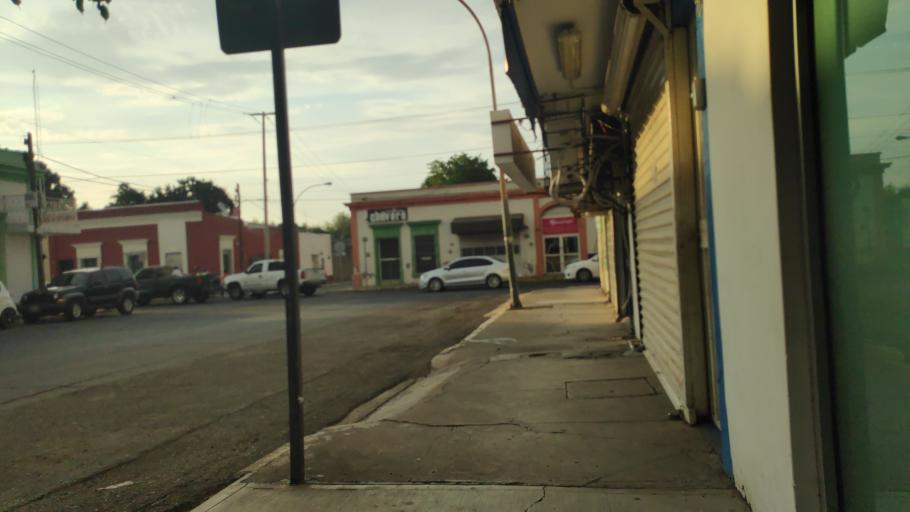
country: MX
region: Sinaloa
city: Culiacan
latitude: 24.8098
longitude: -107.4002
